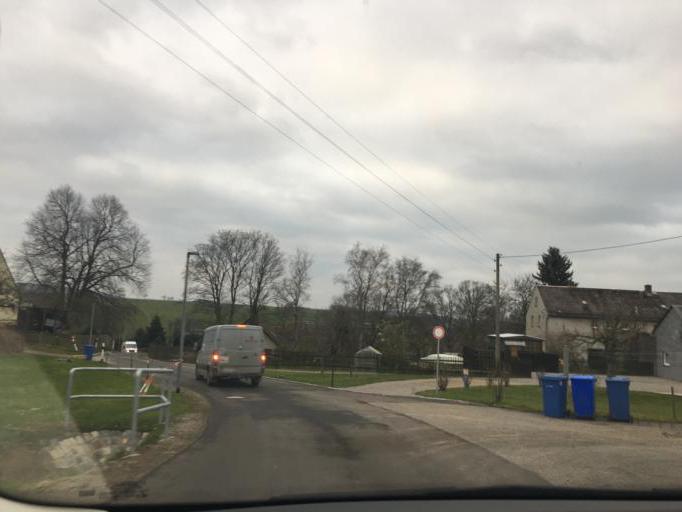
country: DE
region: Saxony
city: Niederfrohna
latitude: 50.8745
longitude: 12.7068
